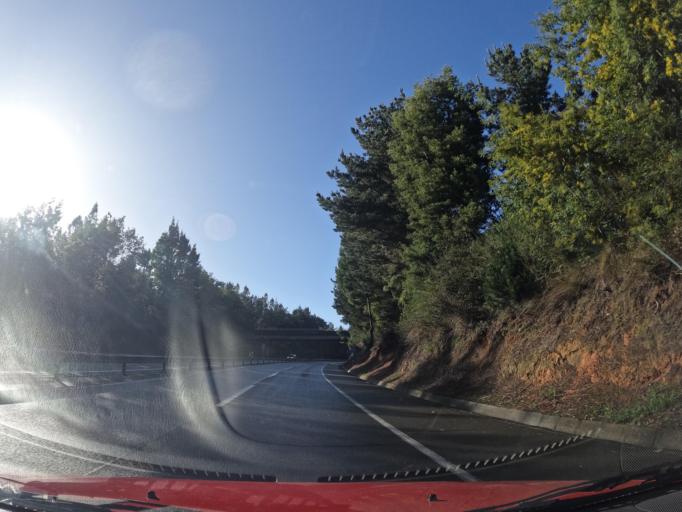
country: CL
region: Biobio
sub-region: Provincia de Concepcion
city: Penco
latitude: -36.7591
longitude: -72.9659
